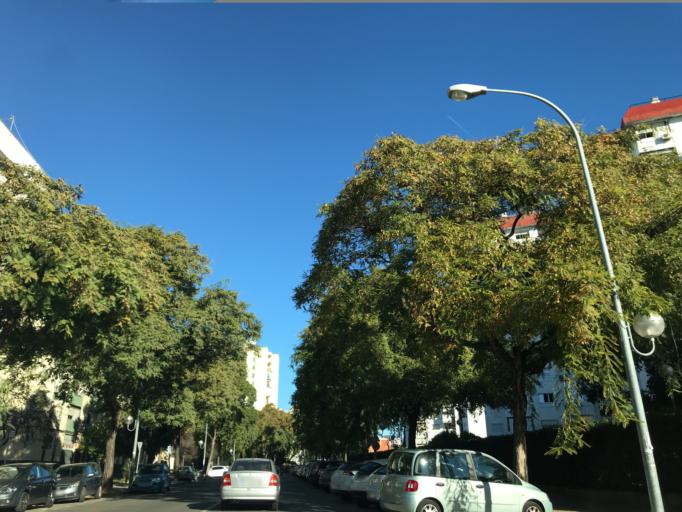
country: ES
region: Andalusia
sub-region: Provincia de Sevilla
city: Sevilla
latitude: 37.3978
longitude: -5.9562
